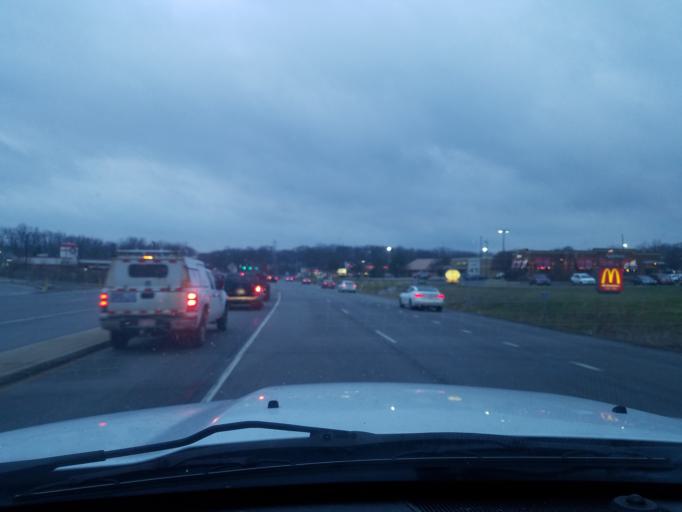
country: US
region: Indiana
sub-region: Huntington County
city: Roanoke
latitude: 41.0319
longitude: -85.2562
